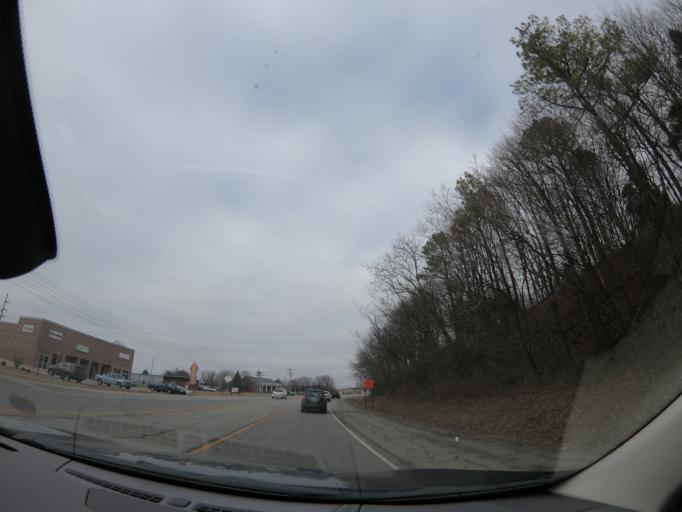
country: US
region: Kentucky
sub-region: Nelson County
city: Bardstown
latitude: 37.8237
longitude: -85.4425
